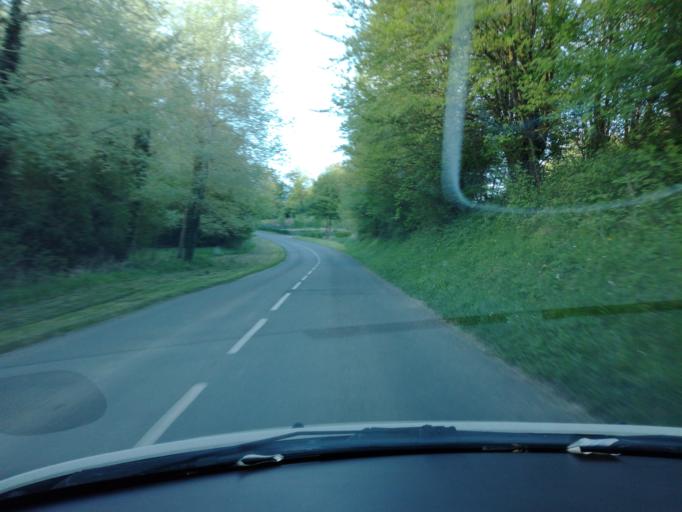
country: FR
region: Picardie
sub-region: Departement de la Somme
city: Poix-de-Picardie
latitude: 49.7849
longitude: 1.9900
